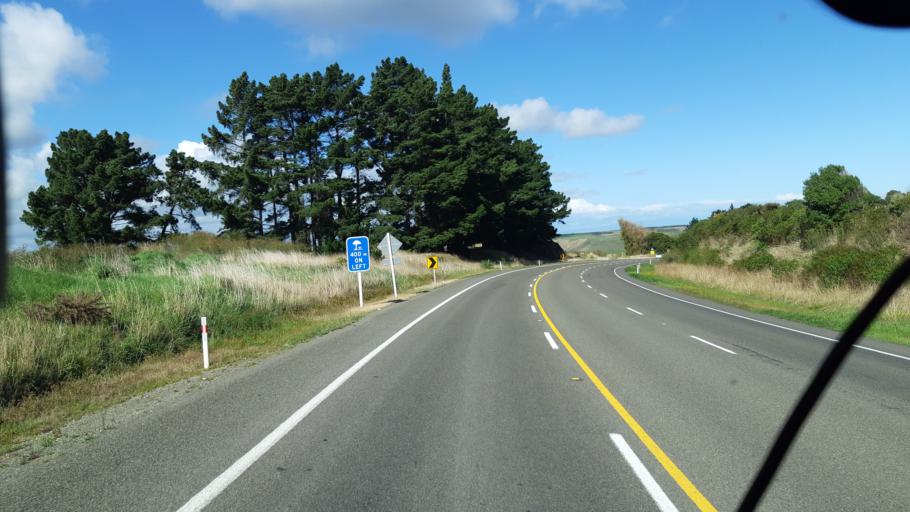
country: NZ
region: Manawatu-Wanganui
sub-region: Wanganui District
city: Wanganui
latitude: -39.9936
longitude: 175.1680
